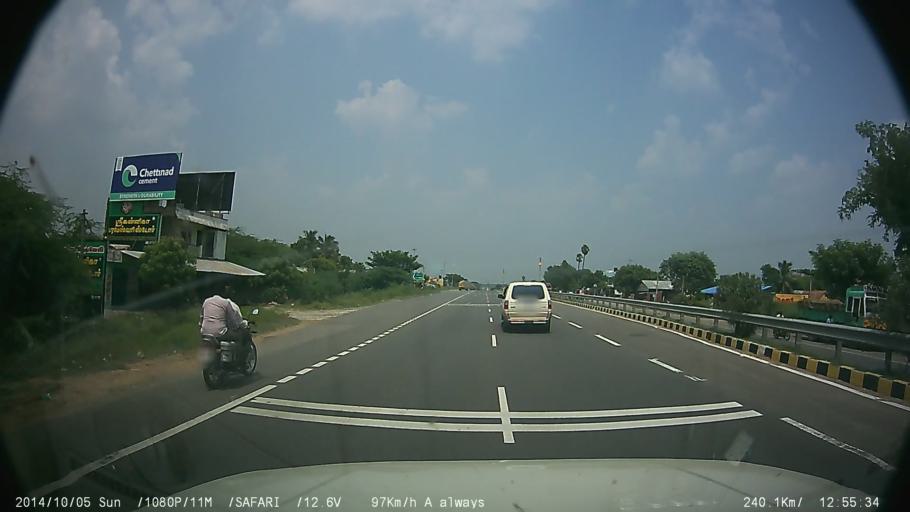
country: IN
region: Tamil Nadu
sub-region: Cuddalore
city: Panruti
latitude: 11.7687
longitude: 79.3868
